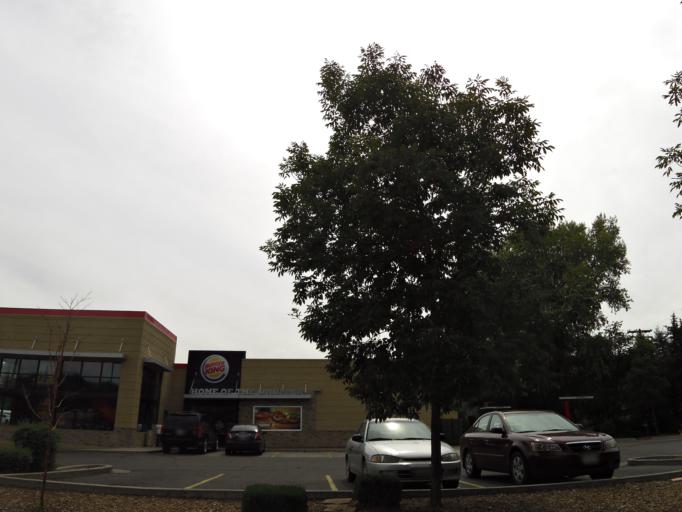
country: US
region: Colorado
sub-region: La Plata County
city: Durango
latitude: 37.2798
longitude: -107.8790
